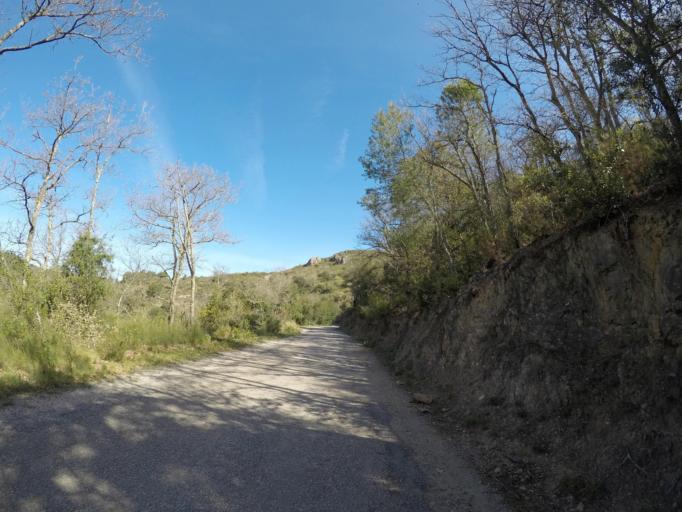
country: FR
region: Languedoc-Roussillon
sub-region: Departement des Pyrenees-Orientales
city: Thuir
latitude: 42.6274
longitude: 2.7047
